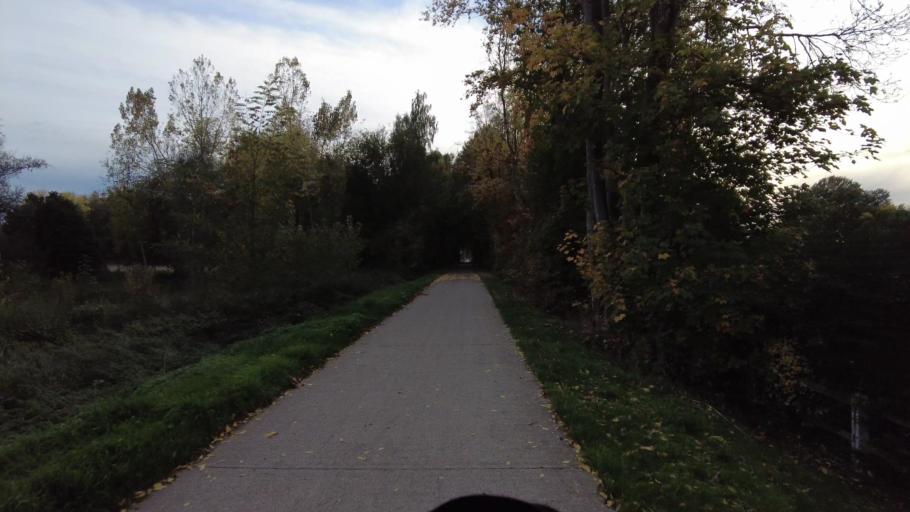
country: BE
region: Flanders
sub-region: Provincie Vlaams-Brabant
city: Hoegaarden
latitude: 50.7629
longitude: 4.8880
